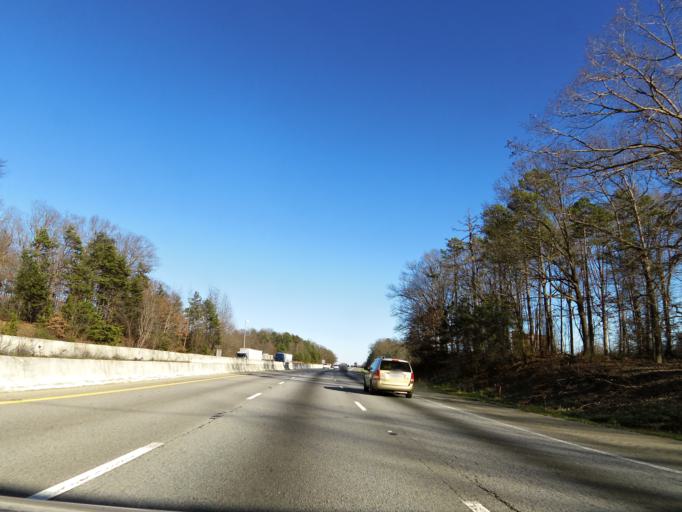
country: US
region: South Carolina
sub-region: Spartanburg County
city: Duncan
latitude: 34.8992
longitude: -82.1476
